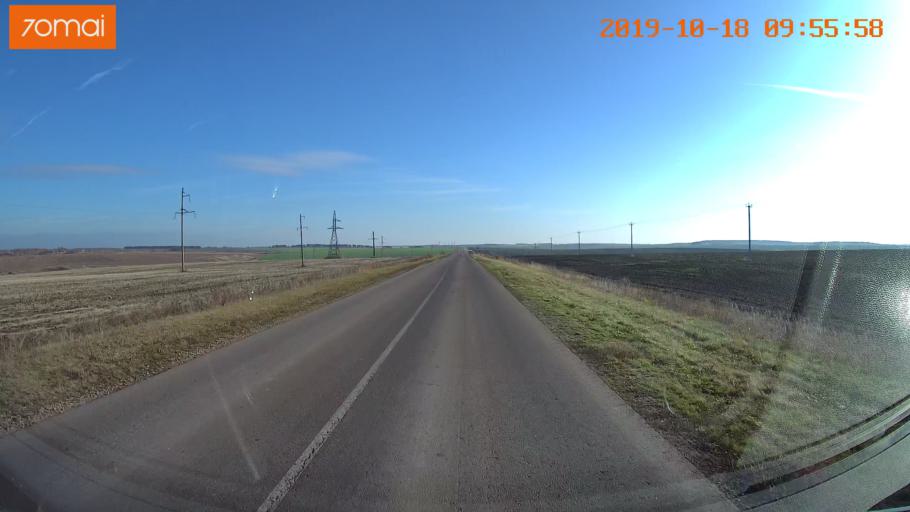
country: RU
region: Tula
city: Kurkino
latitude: 53.3722
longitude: 38.3776
